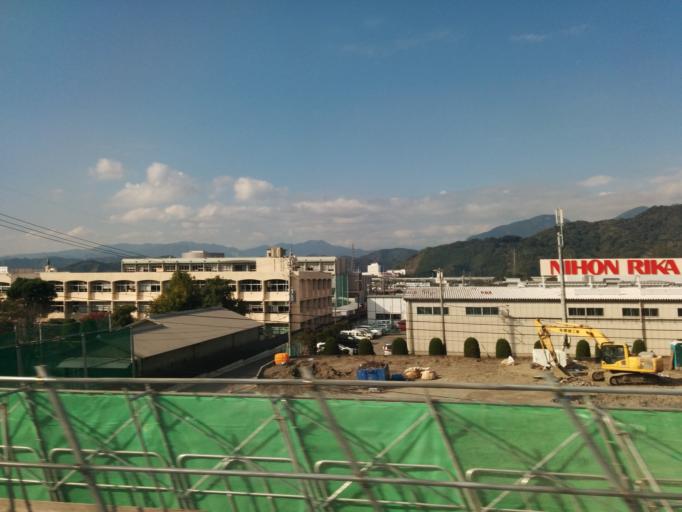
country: JP
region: Shizuoka
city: Shizuoka-shi
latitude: 35.0023
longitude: 138.4405
